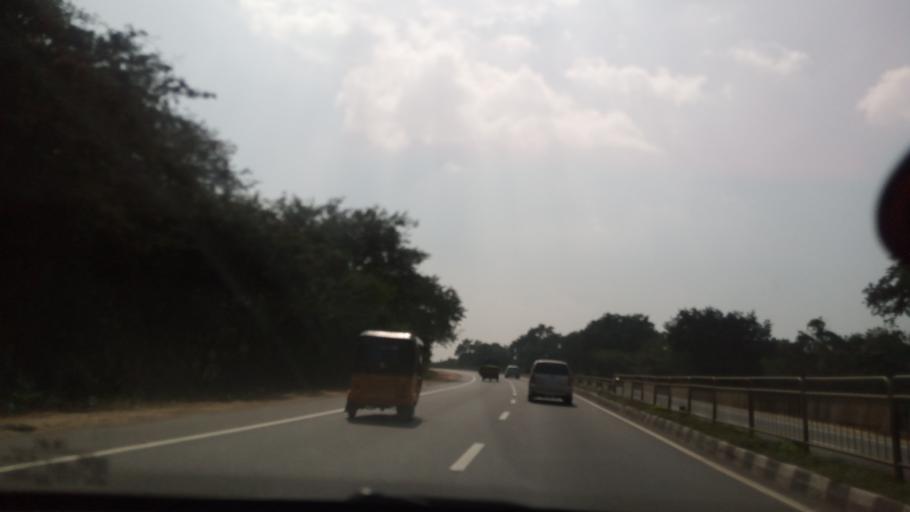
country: IN
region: Tamil Nadu
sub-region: Dharmapuri
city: Dharmapuri
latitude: 11.9821
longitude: 78.0579
